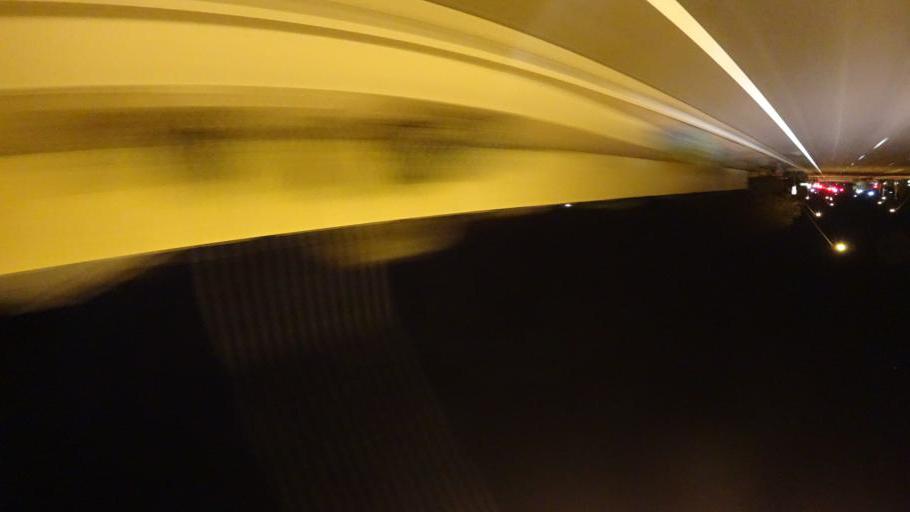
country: US
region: Arizona
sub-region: Maricopa County
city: Gilbert
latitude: 33.4085
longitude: -111.6883
